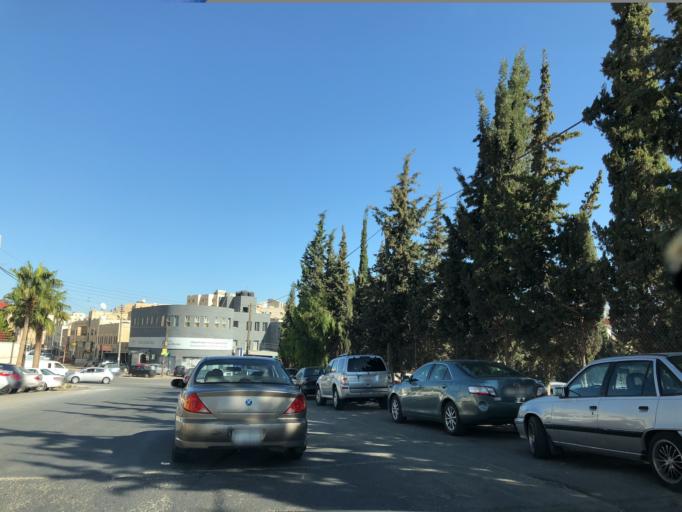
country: JO
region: Amman
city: Wadi as Sir
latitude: 31.9432
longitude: 35.8469
